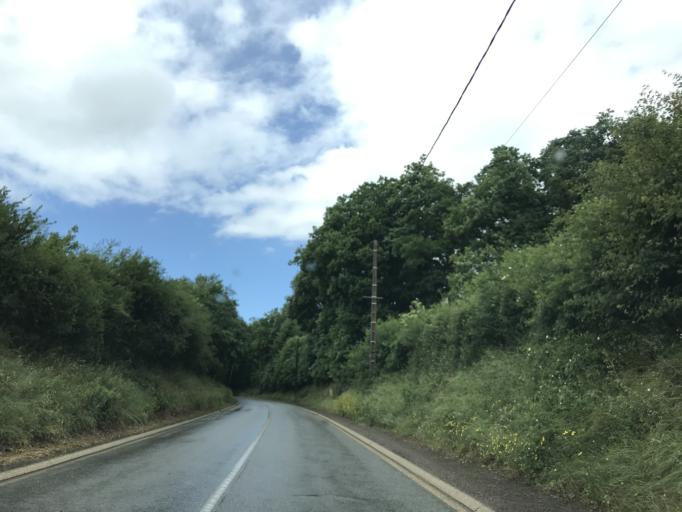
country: FR
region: Haute-Normandie
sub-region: Departement de l'Eure
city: Damville
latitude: 48.8719
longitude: 1.0681
